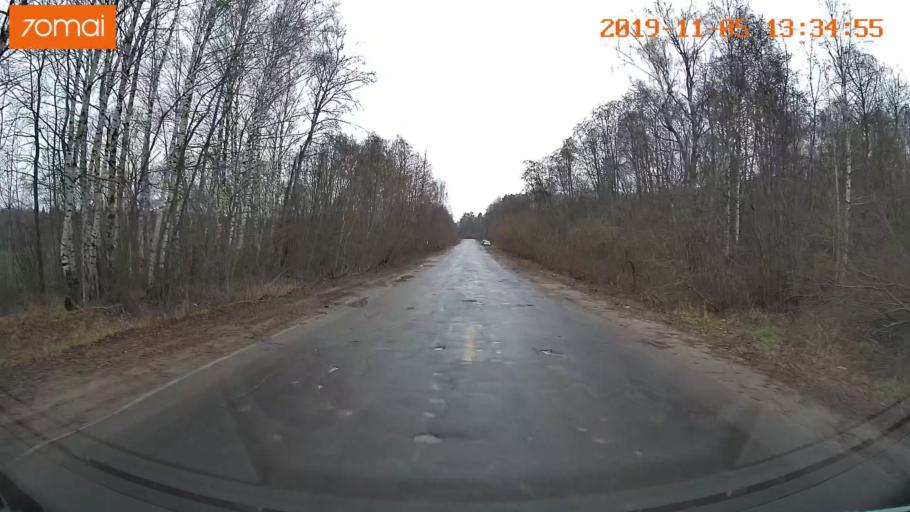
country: RU
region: Ivanovo
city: Shuya
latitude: 56.9042
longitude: 41.3894
